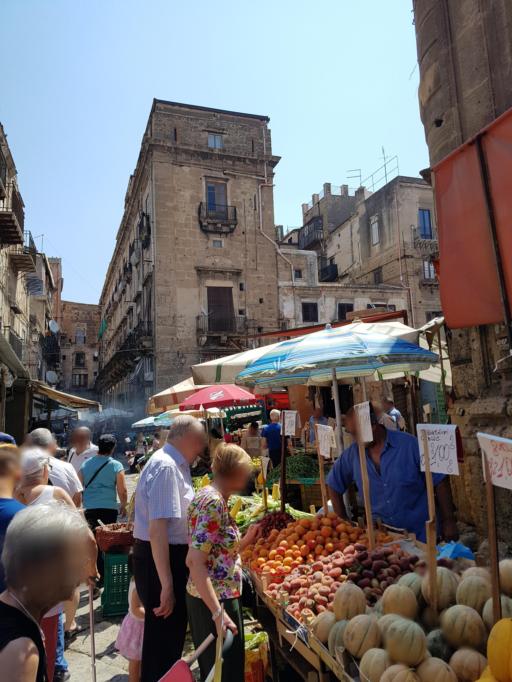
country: IT
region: Sicily
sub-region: Palermo
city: Palermo
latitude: 38.1108
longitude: 13.3636
